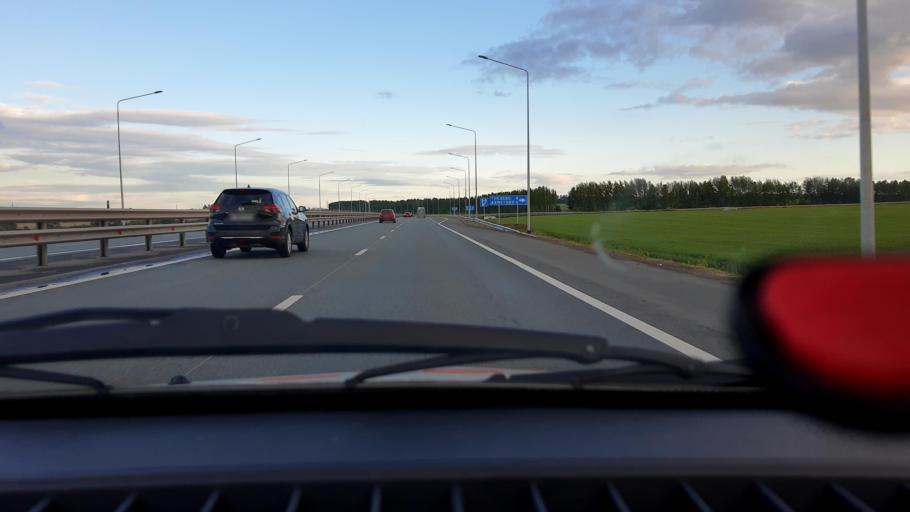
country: RU
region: Bashkortostan
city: Tolbazy
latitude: 54.2124
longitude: 55.8837
